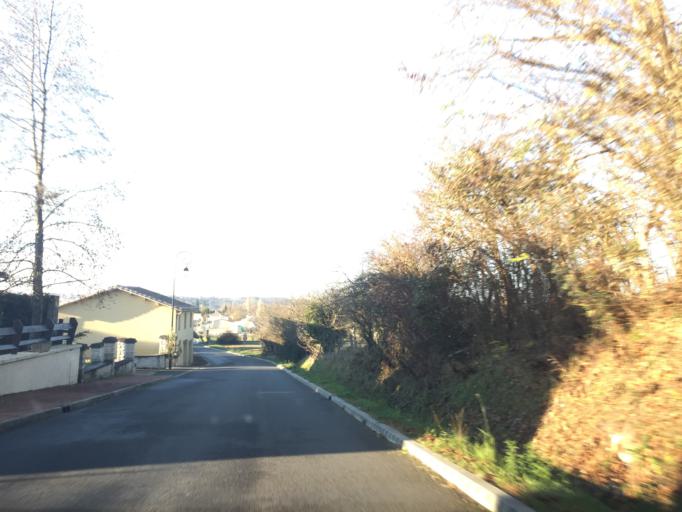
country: FR
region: Aquitaine
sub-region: Departement de la Dordogne
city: Saint-Aulaye
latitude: 45.2574
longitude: 0.1976
